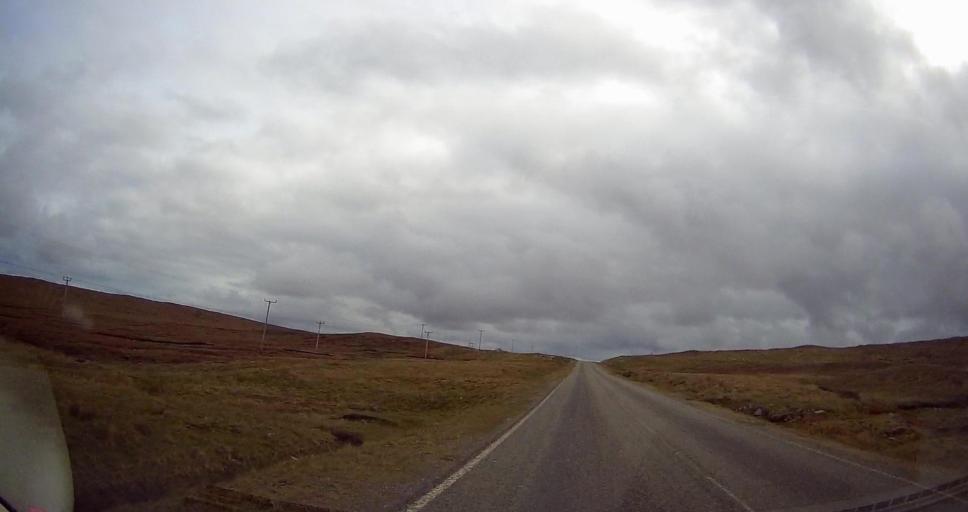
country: GB
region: Scotland
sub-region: Shetland Islands
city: Shetland
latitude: 60.5975
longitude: -1.1419
